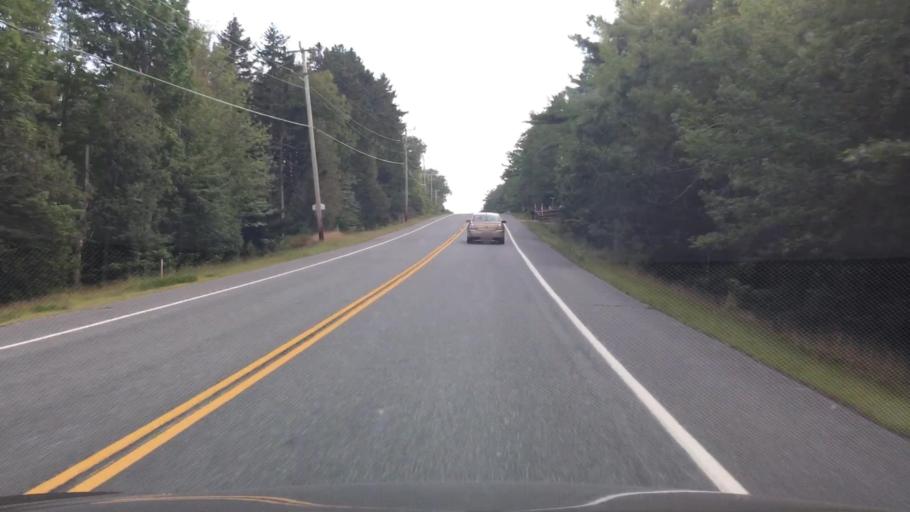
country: US
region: Maine
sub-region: Hancock County
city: Surry
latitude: 44.4529
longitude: -68.5546
